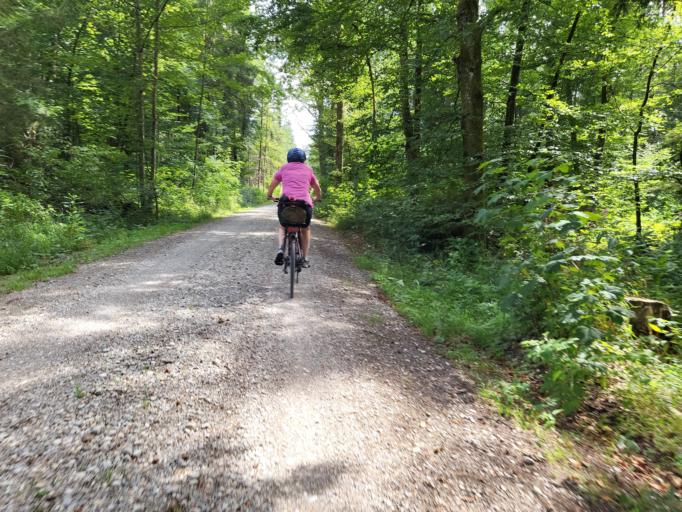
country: DE
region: Bavaria
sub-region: Upper Bavaria
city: Hohenkirchen-Siegertsbrunn
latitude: 48.0401
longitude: 11.7467
